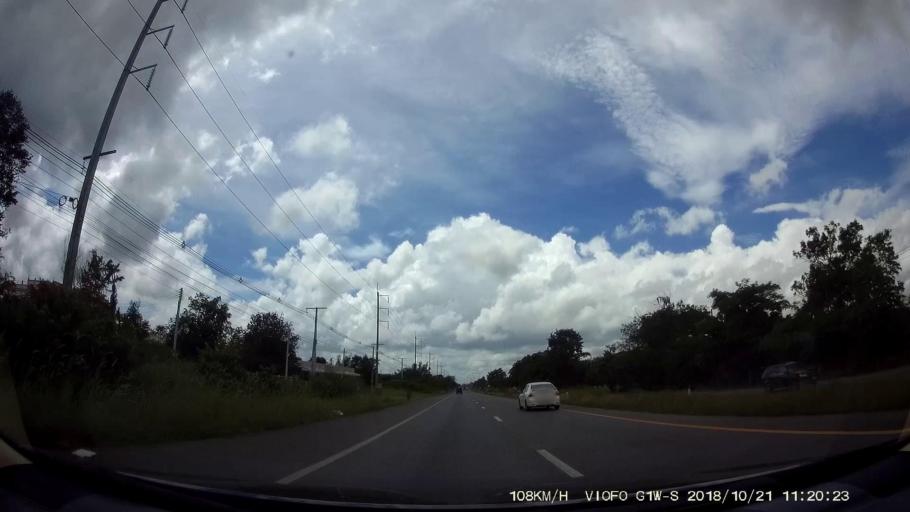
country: TH
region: Chaiyaphum
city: Chaiyaphum
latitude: 15.8571
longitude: 102.0754
